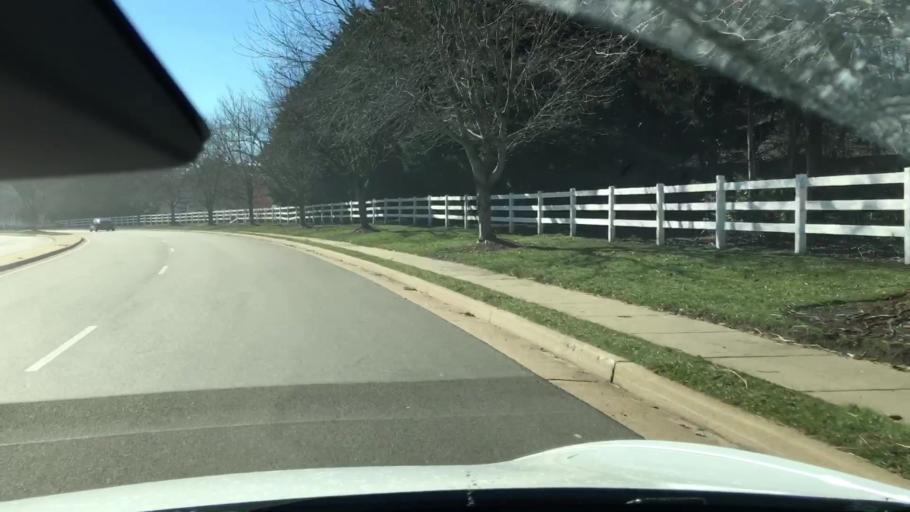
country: US
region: Virginia
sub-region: Henrico County
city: Glen Allen
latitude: 37.6695
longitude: -77.4667
